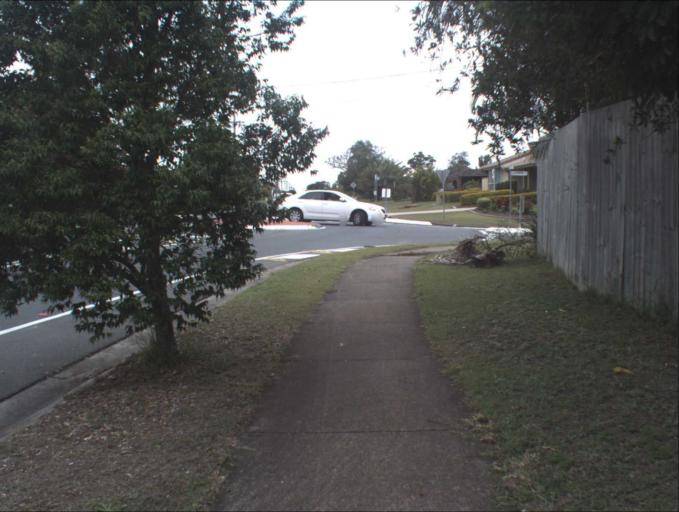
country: AU
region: Queensland
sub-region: Brisbane
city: Sunnybank Hills
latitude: -27.6587
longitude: 153.0234
